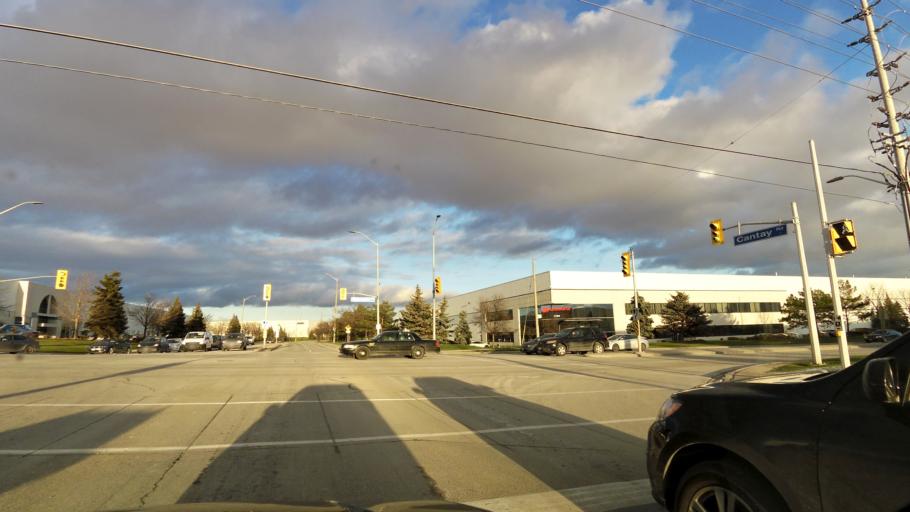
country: CA
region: Ontario
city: Mississauga
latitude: 43.6210
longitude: -79.6960
